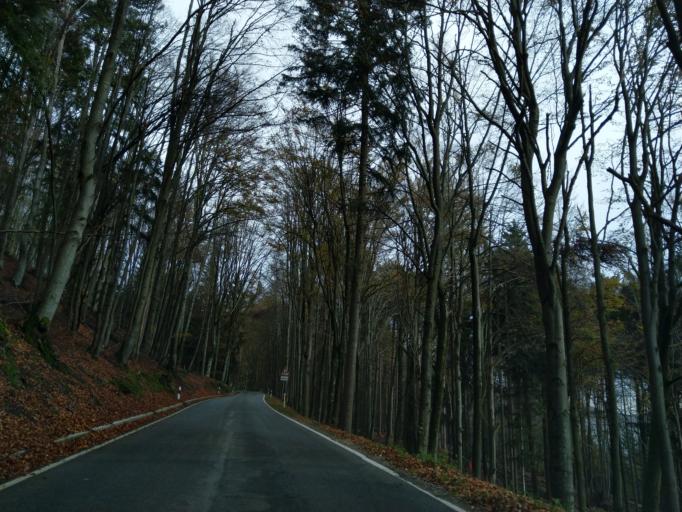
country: DE
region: Bavaria
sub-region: Lower Bavaria
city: Zenting
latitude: 48.7927
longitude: 13.2369
